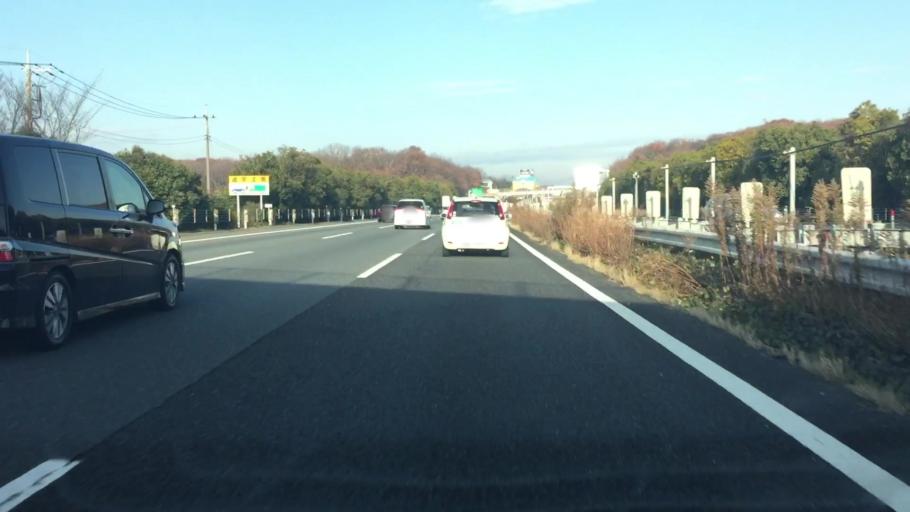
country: JP
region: Saitama
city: Honjo
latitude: 36.2065
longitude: 139.1733
